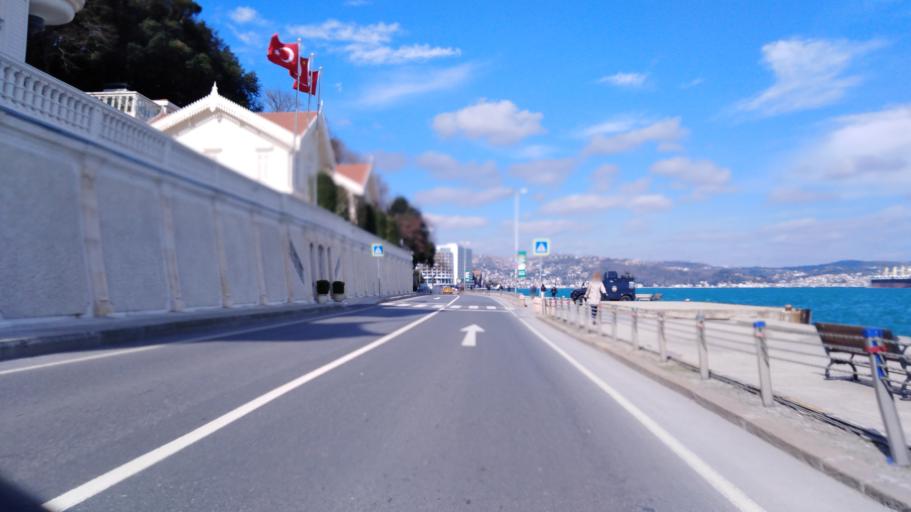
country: TR
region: Istanbul
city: Sisli
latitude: 41.1342
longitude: 29.0623
